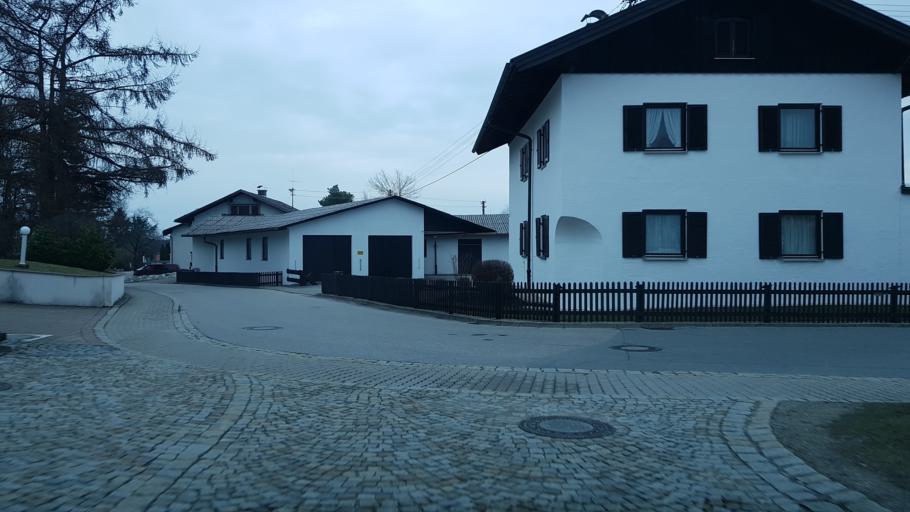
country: DE
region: Bavaria
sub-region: Upper Bavaria
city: Bernau am Chiemsee
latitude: 47.8124
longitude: 12.3784
